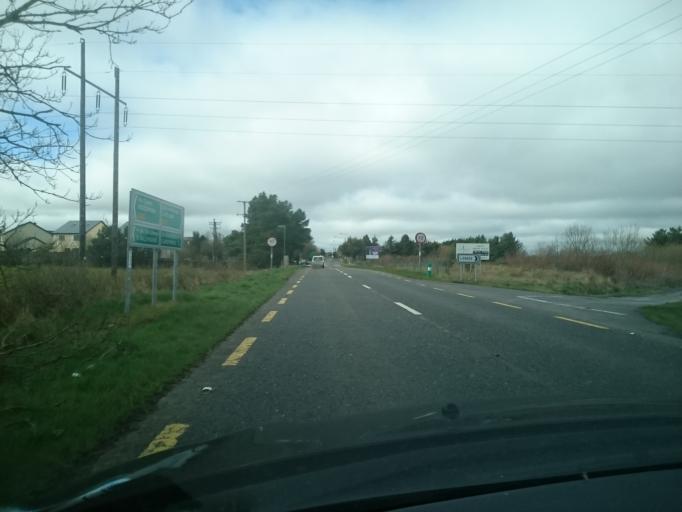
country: IE
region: Connaught
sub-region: Maigh Eo
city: Claremorris
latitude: 53.7236
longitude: -8.9710
